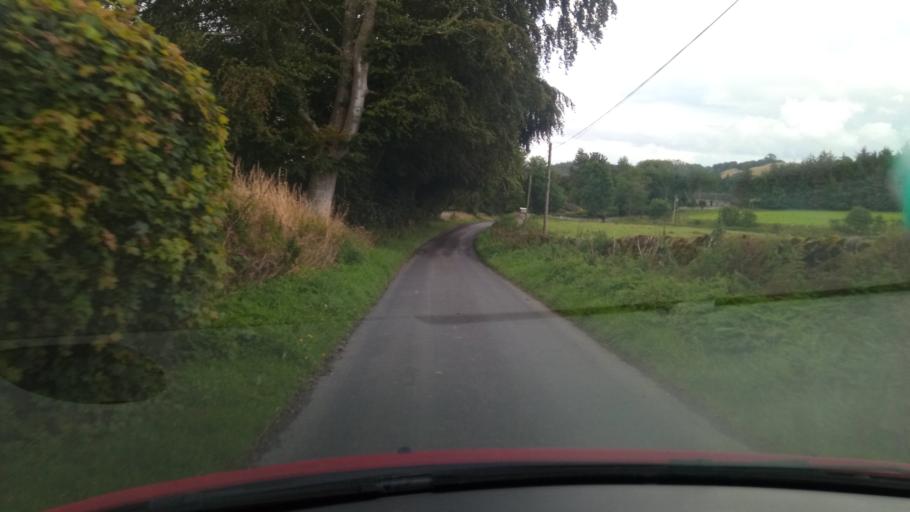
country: GB
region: Scotland
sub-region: The Scottish Borders
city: Hawick
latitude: 55.4199
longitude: -2.7523
